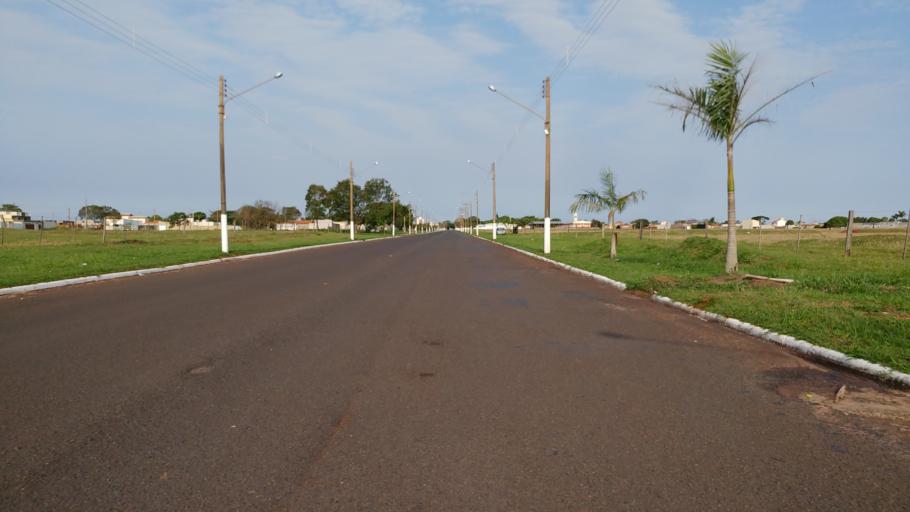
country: BR
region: Sao Paulo
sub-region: Paraguacu Paulista
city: Paraguacu Paulista
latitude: -22.4097
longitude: -50.5941
